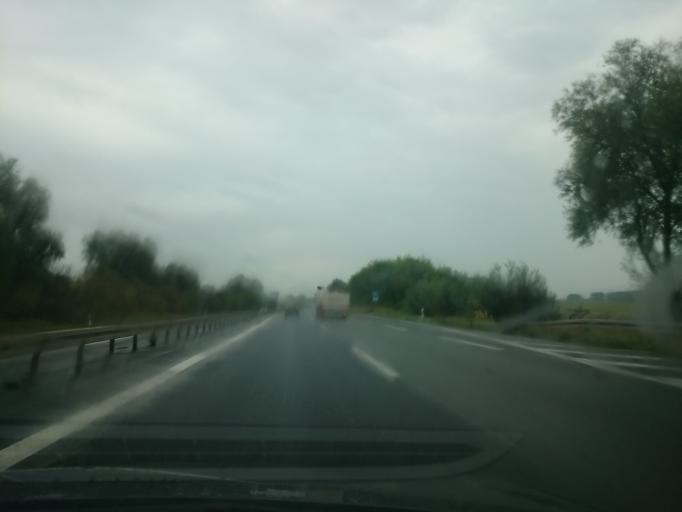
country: DE
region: Brandenburg
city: Wustermark
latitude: 52.5353
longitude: 12.9662
